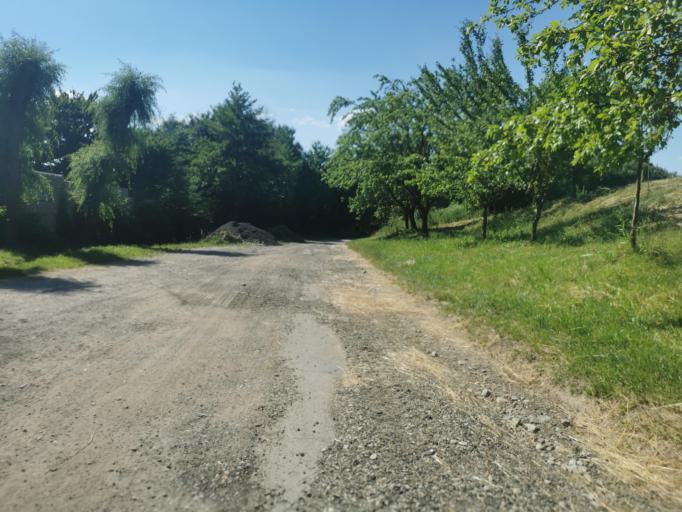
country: SK
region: Trnavsky
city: Smolenice
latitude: 48.5536
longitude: 17.3555
